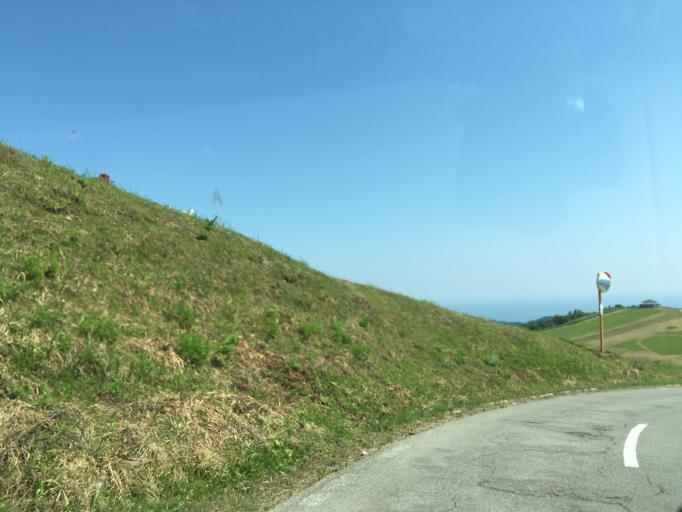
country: JP
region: Akita
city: Tenno
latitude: 39.9292
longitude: 139.8741
